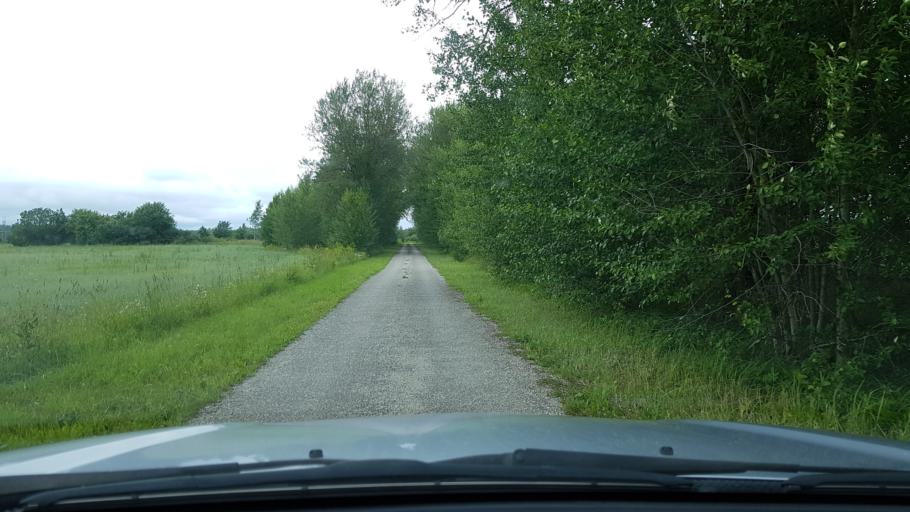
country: EE
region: Ida-Virumaa
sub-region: Narva-Joesuu linn
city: Narva-Joesuu
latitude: 59.3417
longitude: 27.9408
